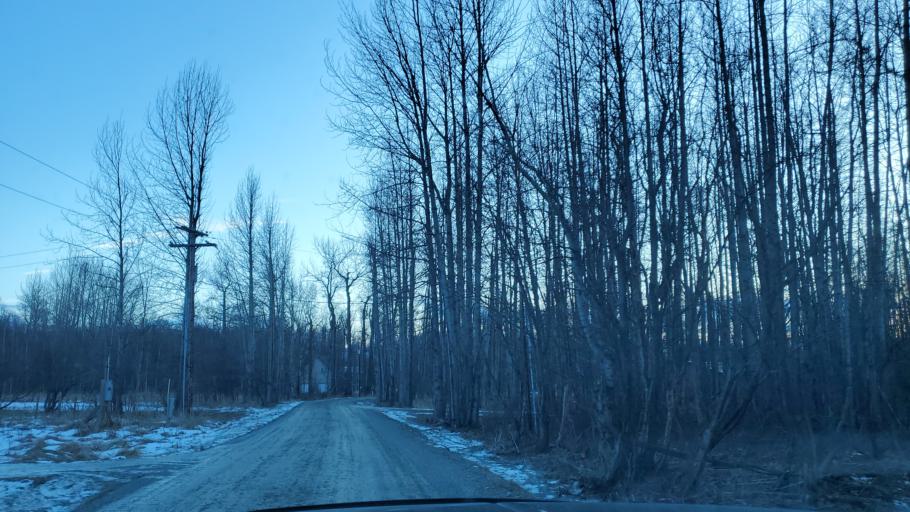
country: US
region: Alaska
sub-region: Matanuska-Susitna Borough
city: Lakes
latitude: 61.6648
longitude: -149.3360
